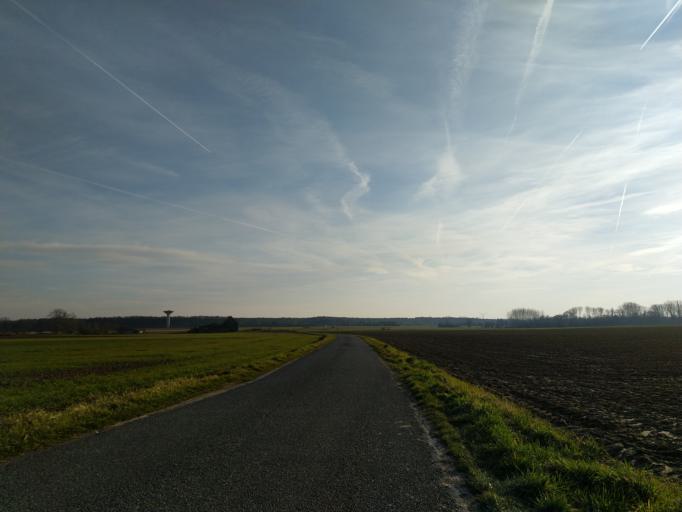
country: BE
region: Wallonia
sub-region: Province du Hainaut
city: Jurbise
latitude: 50.5222
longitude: 3.9093
